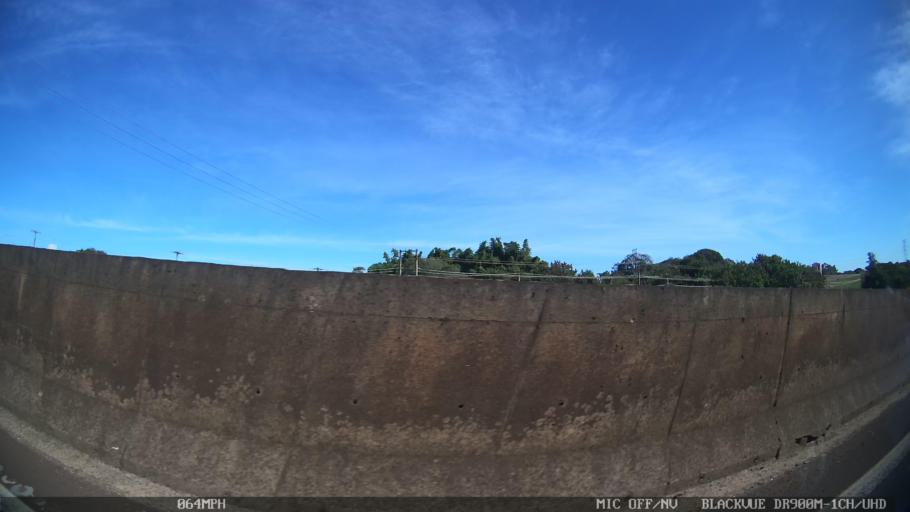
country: BR
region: Sao Paulo
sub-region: Leme
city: Leme
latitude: -22.1932
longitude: -47.3974
